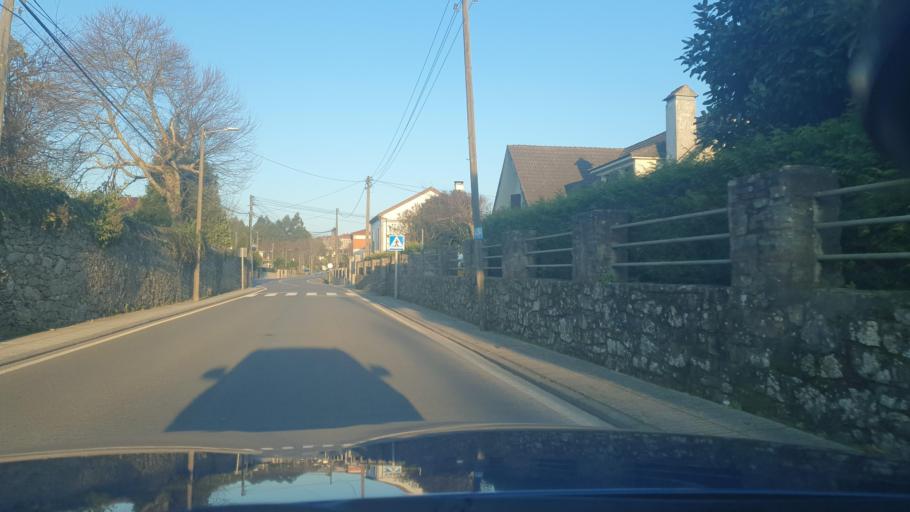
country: ES
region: Galicia
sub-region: Provincia da Coruna
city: Santiago de Compostela
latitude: 42.8394
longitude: -8.5889
